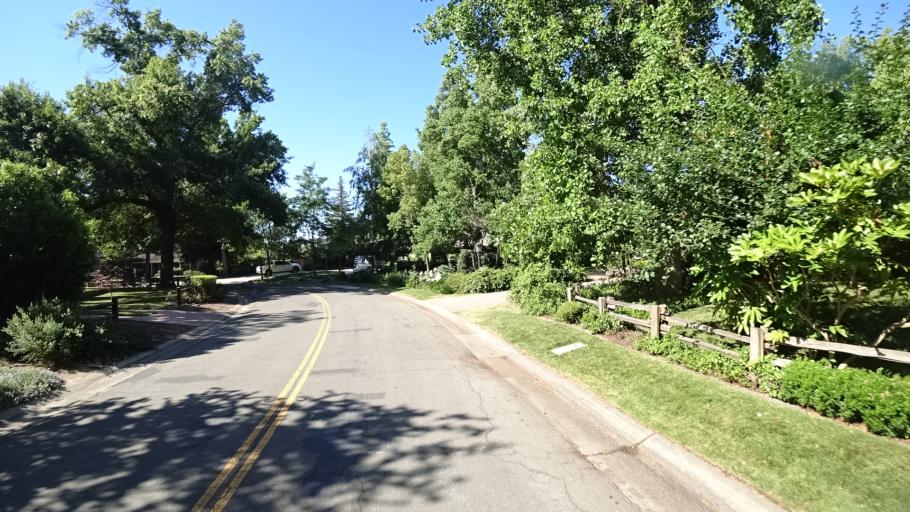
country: US
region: California
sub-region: Sacramento County
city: Sacramento
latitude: 38.5337
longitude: -121.5012
